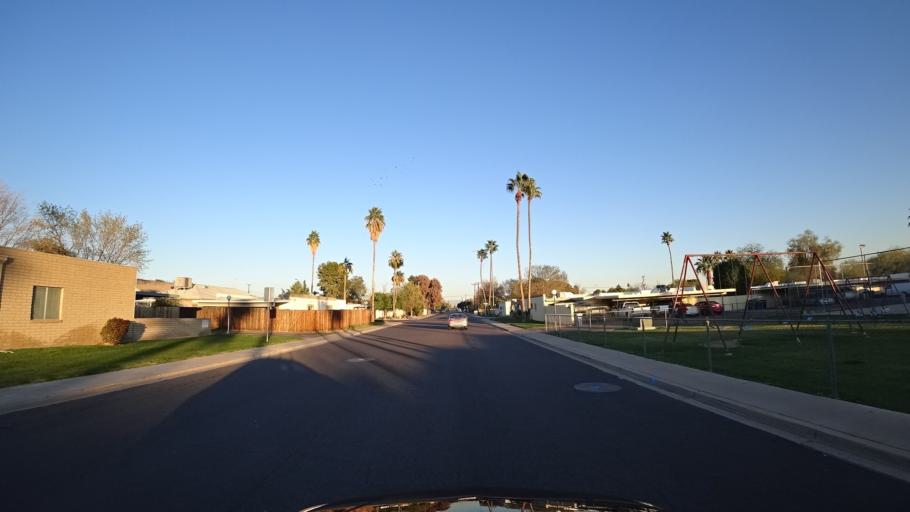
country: US
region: Arizona
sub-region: Maricopa County
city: Mesa
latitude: 33.4260
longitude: -111.8196
